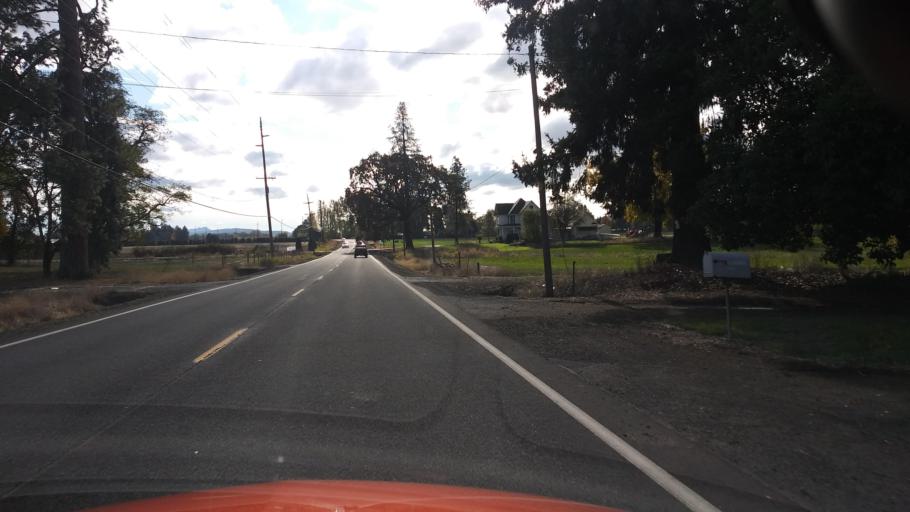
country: US
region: Oregon
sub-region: Washington County
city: Banks
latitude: 45.5872
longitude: -123.1144
